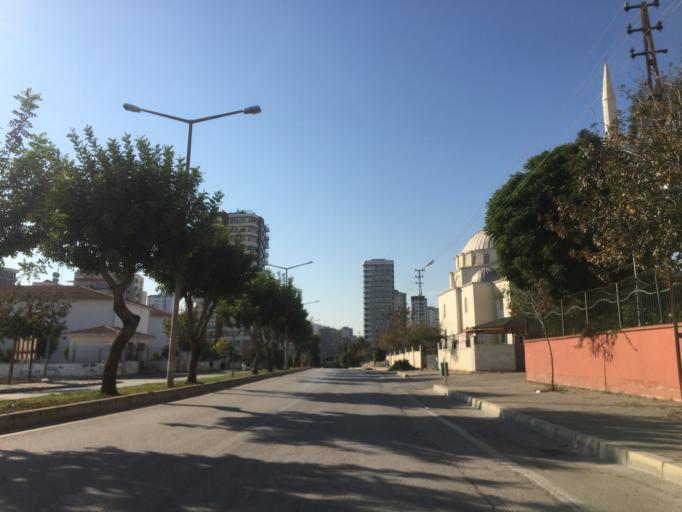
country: TR
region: Adana
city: Seyhan
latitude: 37.0289
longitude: 35.2642
